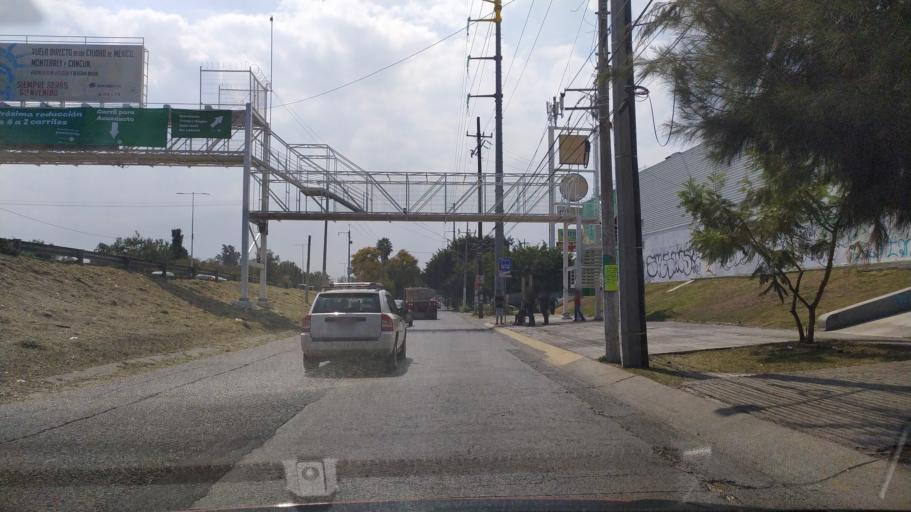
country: MX
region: Jalisco
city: Zapopan2
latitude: 20.7355
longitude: -103.4083
